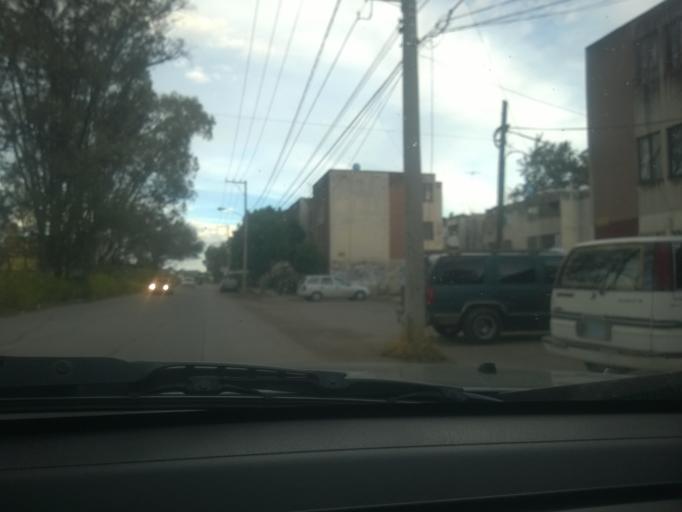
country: MX
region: Guanajuato
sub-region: Leon
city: Medina
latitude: 21.1296
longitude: -101.6381
